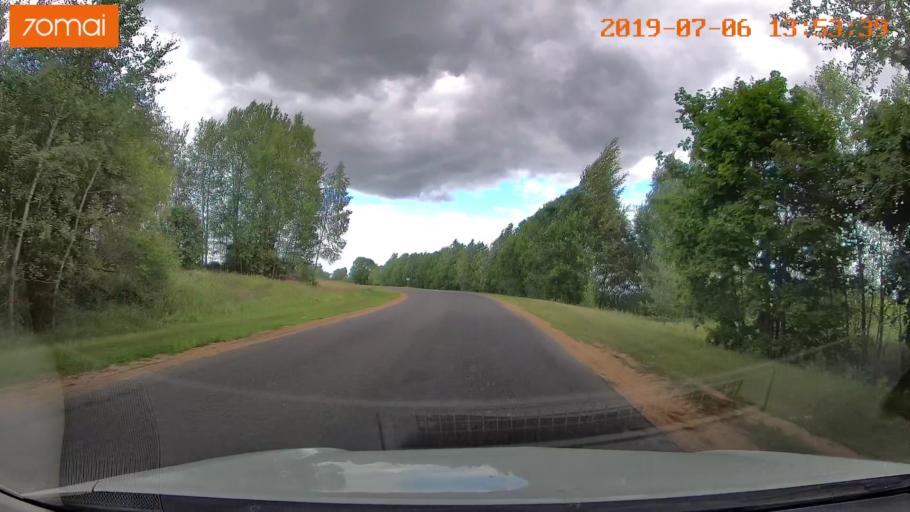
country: BY
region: Minsk
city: Ivyanyets
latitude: 53.7367
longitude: 26.8248
